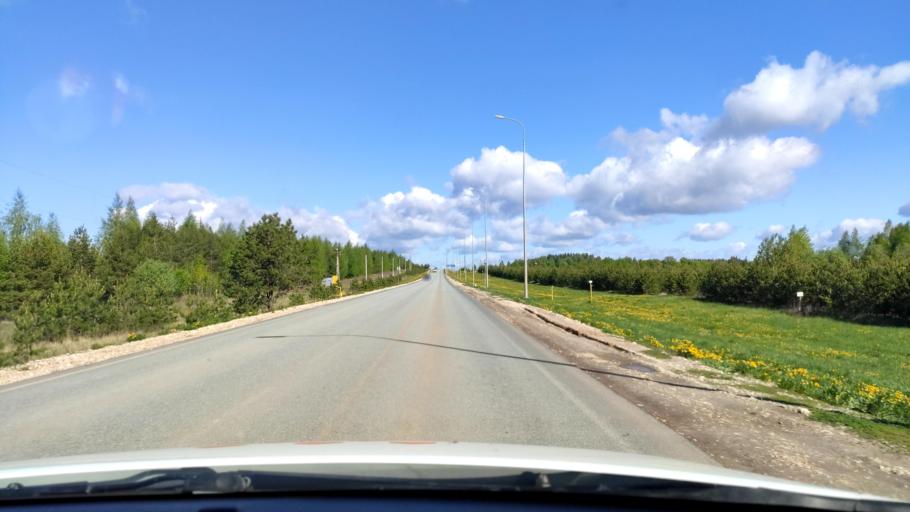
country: RU
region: Tatarstan
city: Sviyazhsk
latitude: 55.7262
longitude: 48.7477
